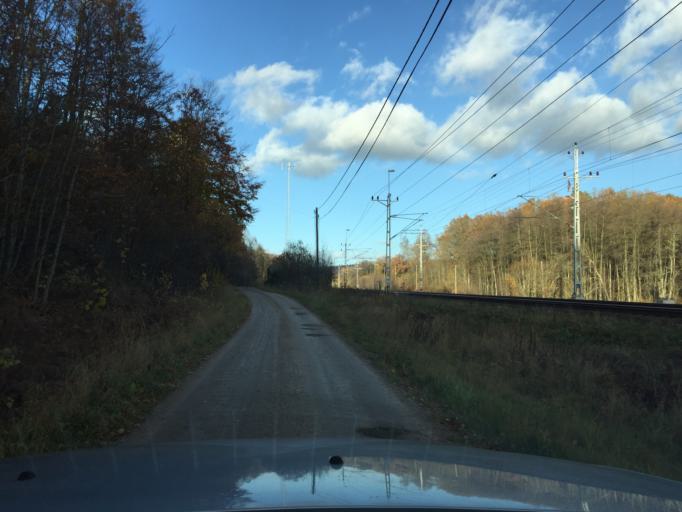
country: SE
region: Skane
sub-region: Hassleholms Kommun
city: Tormestorp
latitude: 56.0732
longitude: 13.7361
